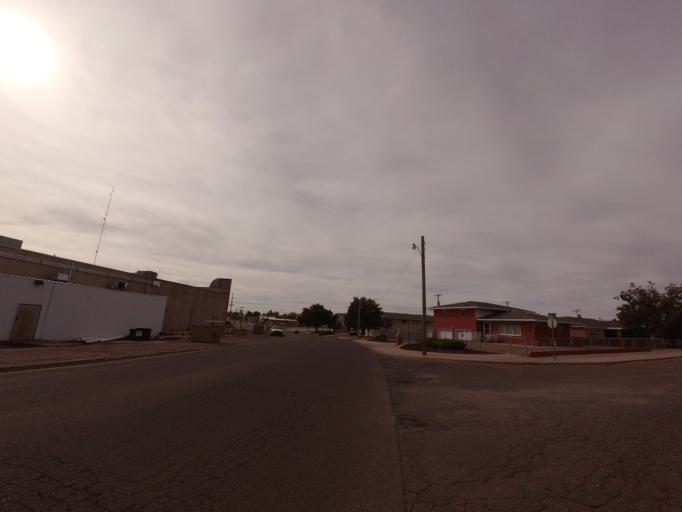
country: US
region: New Mexico
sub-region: Curry County
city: Clovis
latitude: 34.4204
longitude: -103.2094
